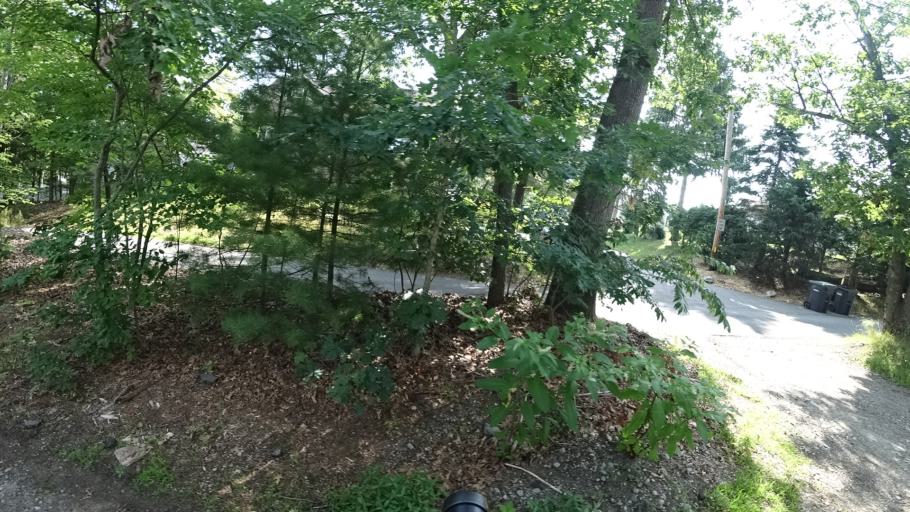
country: US
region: Massachusetts
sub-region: Norfolk County
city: Dedham
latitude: 42.2378
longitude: -71.1702
